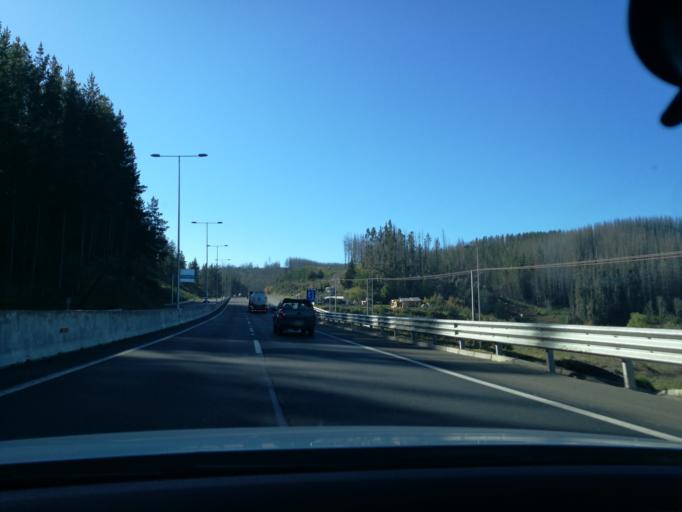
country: CL
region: Biobio
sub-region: Provincia de Concepcion
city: Penco
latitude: -36.8568
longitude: -72.8682
